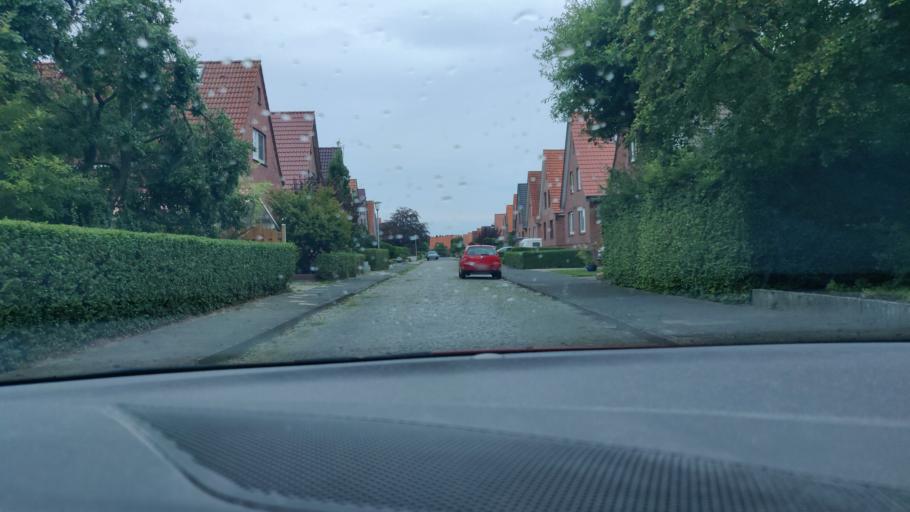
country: DE
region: Lower Saxony
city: Cuxhaven
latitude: 53.8800
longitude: 8.6642
